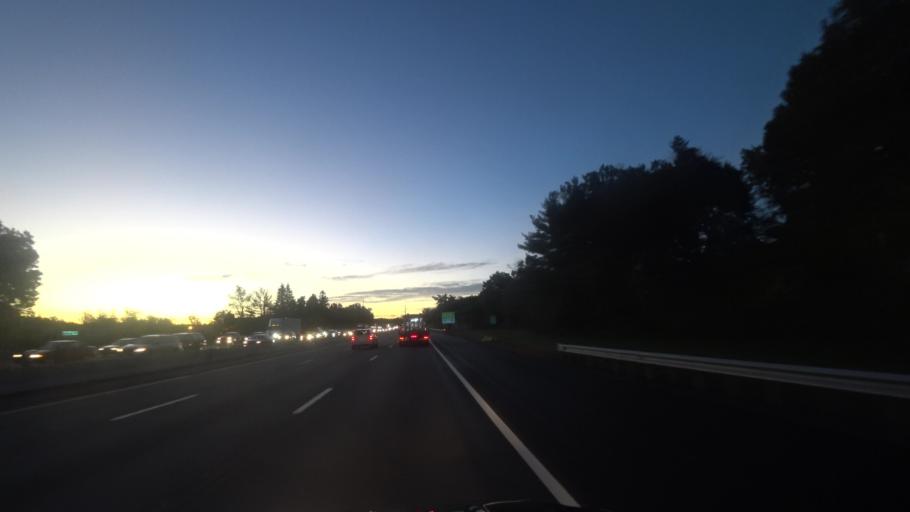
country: US
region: Massachusetts
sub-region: Essex County
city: Lynnfield
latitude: 42.5171
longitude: -71.0499
